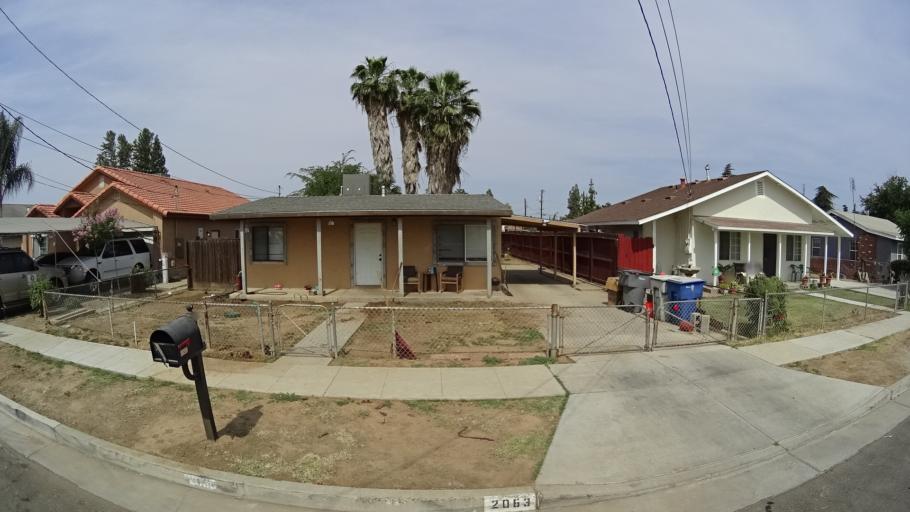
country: US
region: California
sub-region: Fresno County
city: West Park
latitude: 36.7658
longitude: -119.8741
